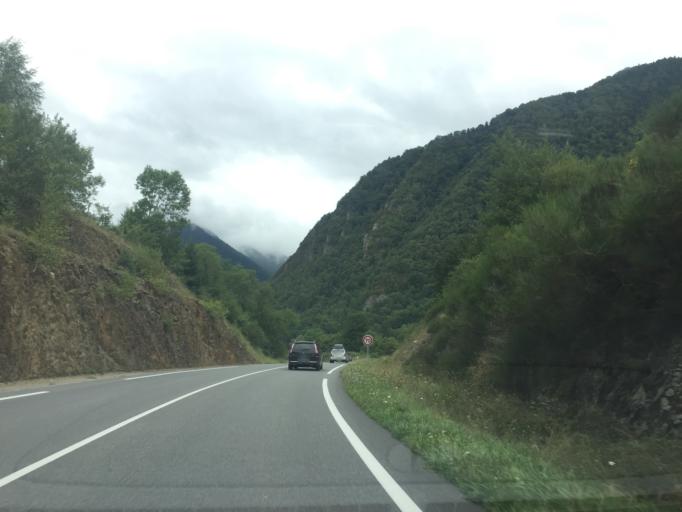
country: FR
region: Midi-Pyrenees
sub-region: Departement des Hautes-Pyrenees
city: Saint-Lary-Soulan
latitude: 42.8861
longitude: 0.3521
